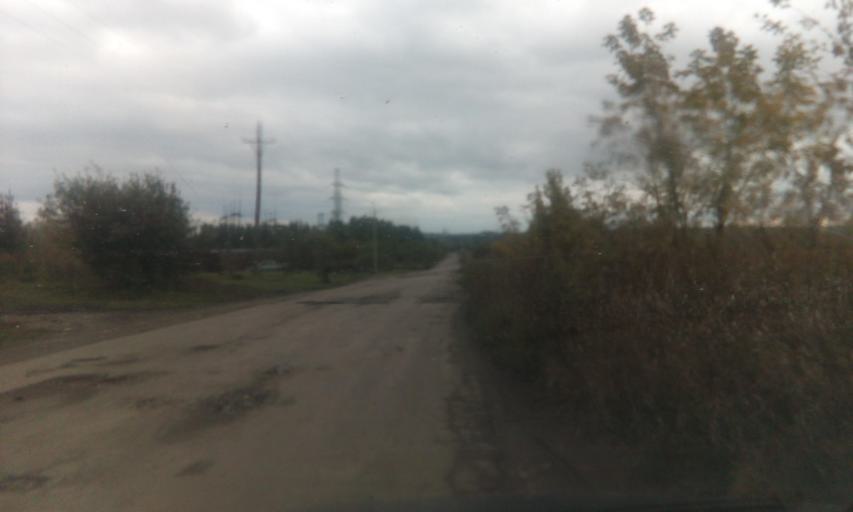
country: RU
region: Tula
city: Gritsovskiy
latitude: 54.1329
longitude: 38.1584
